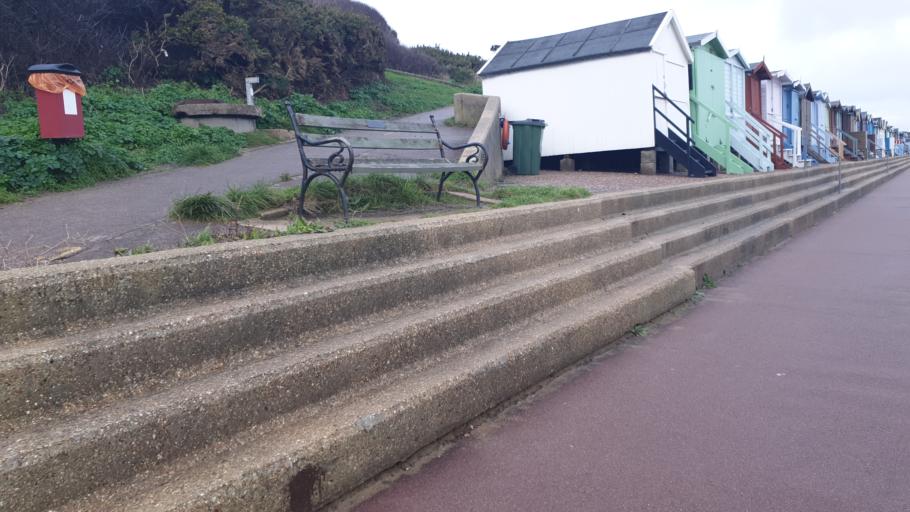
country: GB
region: England
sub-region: Essex
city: Frinton-on-Sea
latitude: 51.8312
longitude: 1.2516
